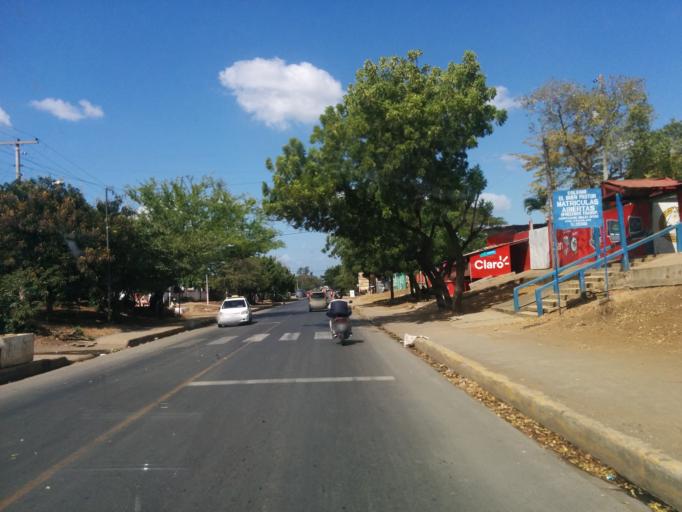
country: NI
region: Managua
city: Tipitapa
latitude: 12.1827
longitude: -86.0962
